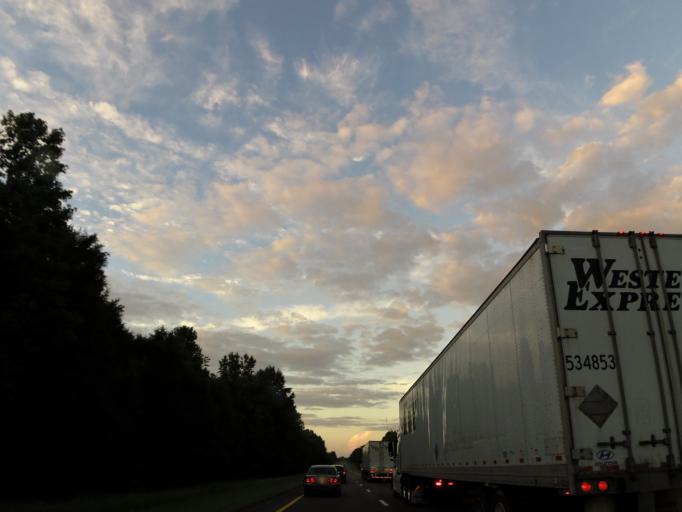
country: US
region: Tennessee
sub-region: Monroe County
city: Sweetwater
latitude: 35.6068
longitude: -84.5083
